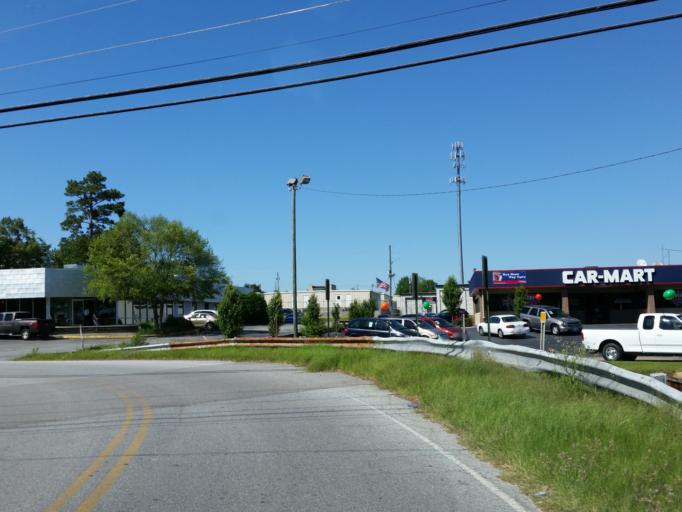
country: US
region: Georgia
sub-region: Lowndes County
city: Remerton
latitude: 30.8785
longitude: -83.2949
